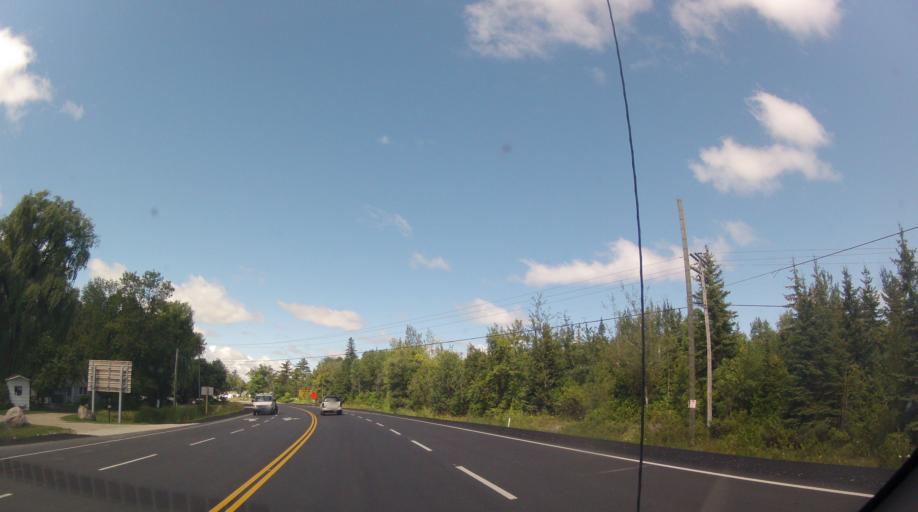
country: CA
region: Ontario
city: Wasaga Beach
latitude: 44.4678
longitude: -80.1097
